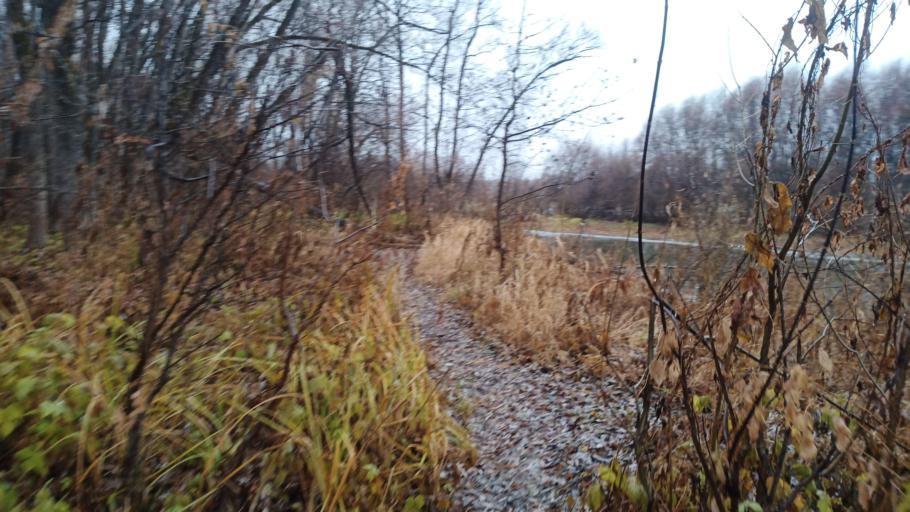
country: RU
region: Altai Krai
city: Nauchnyy Gorodok
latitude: 53.4257
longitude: 83.5017
